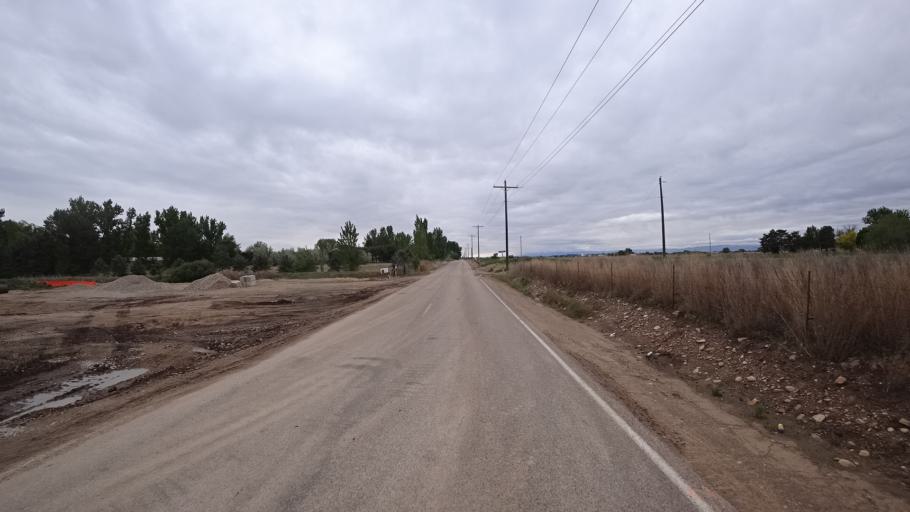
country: US
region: Idaho
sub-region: Ada County
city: Star
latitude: 43.6427
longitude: -116.4734
